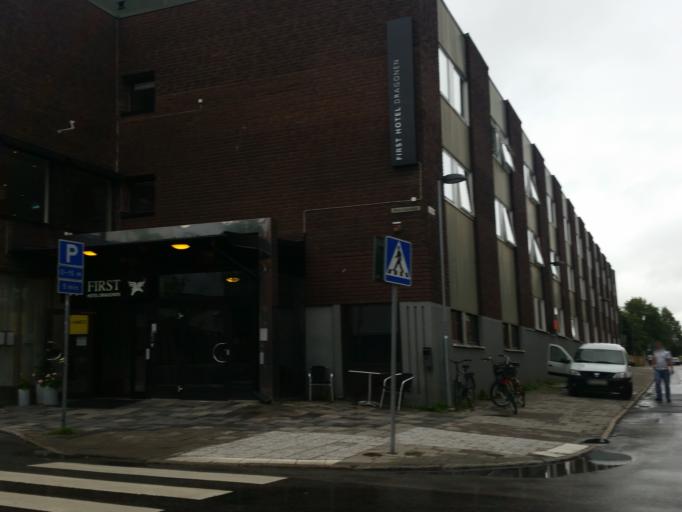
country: SE
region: Vaesterbotten
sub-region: Umea Kommun
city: Umea
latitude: 63.8291
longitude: 20.2602
